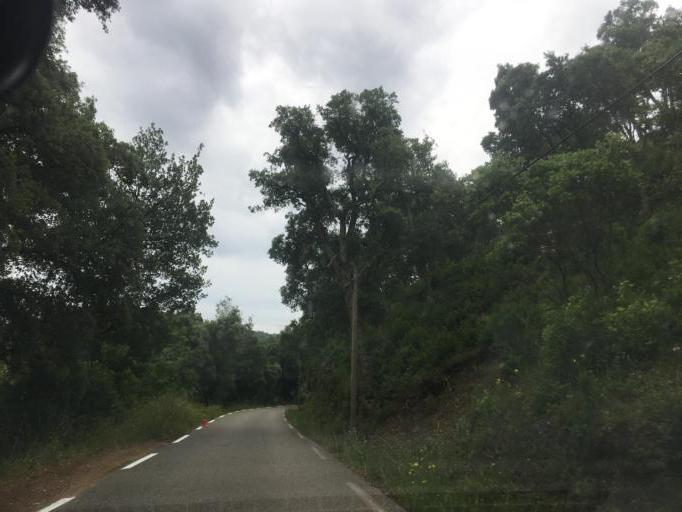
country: FR
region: Provence-Alpes-Cote d'Azur
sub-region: Departement du Var
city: La Londe-les-Maures
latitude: 43.1857
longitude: 6.2132
